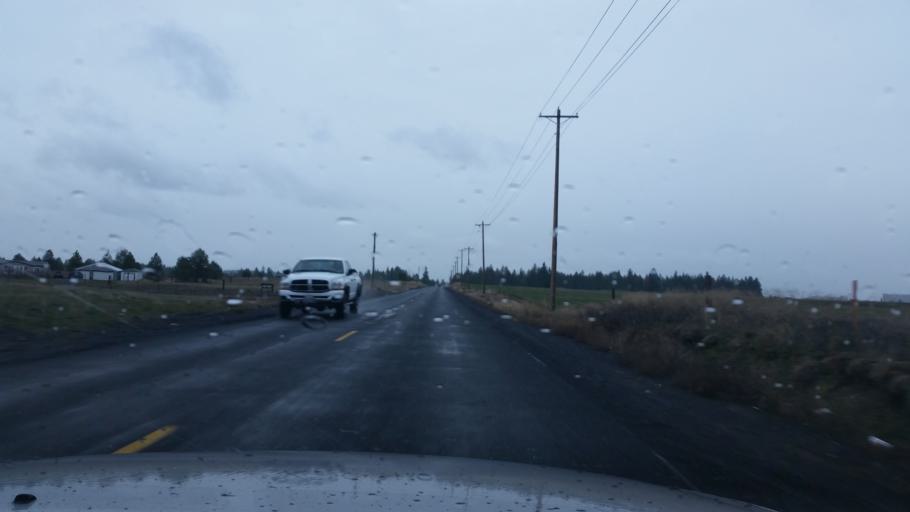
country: US
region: Washington
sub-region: Spokane County
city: Airway Heights
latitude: 47.6719
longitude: -117.5975
